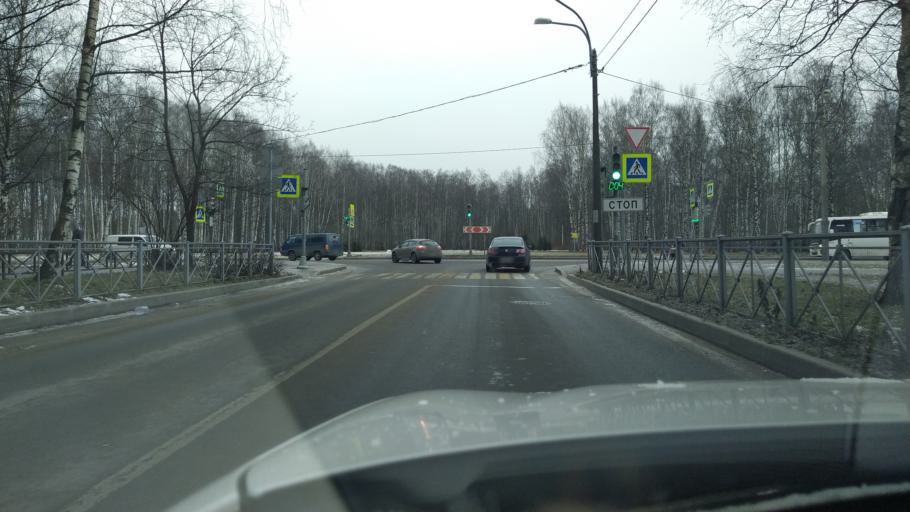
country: RU
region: Leningrad
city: Kalininskiy
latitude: 60.0003
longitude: 30.3941
